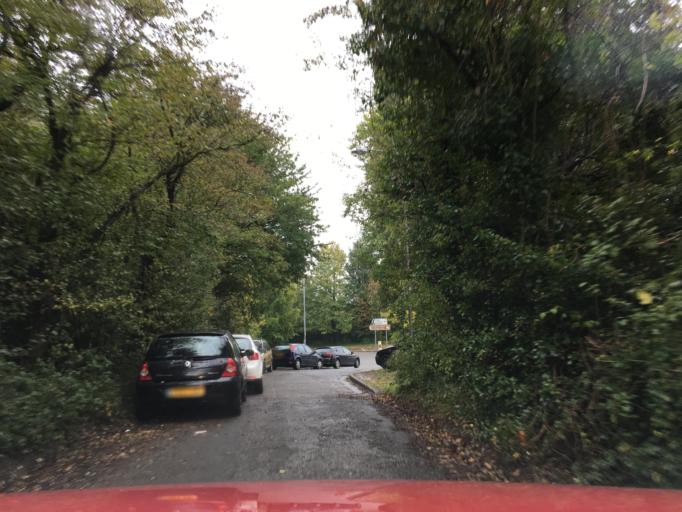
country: GB
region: Wales
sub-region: Monmouthshire
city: Magor
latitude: 51.5848
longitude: -2.8396
